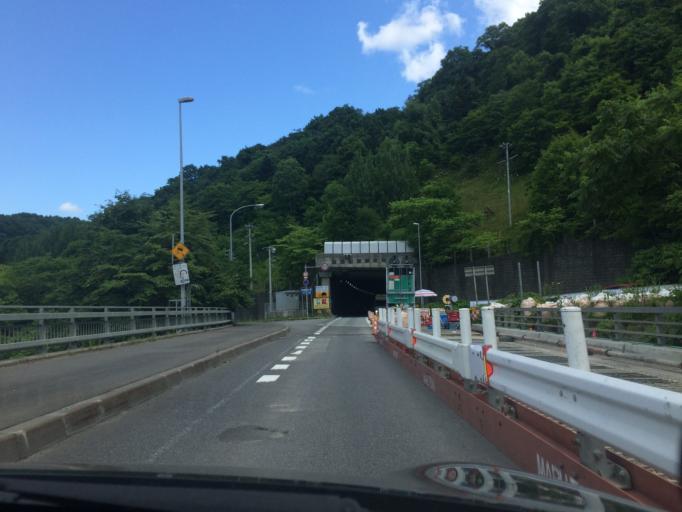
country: JP
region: Hokkaido
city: Fukagawa
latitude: 43.7301
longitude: 142.1980
